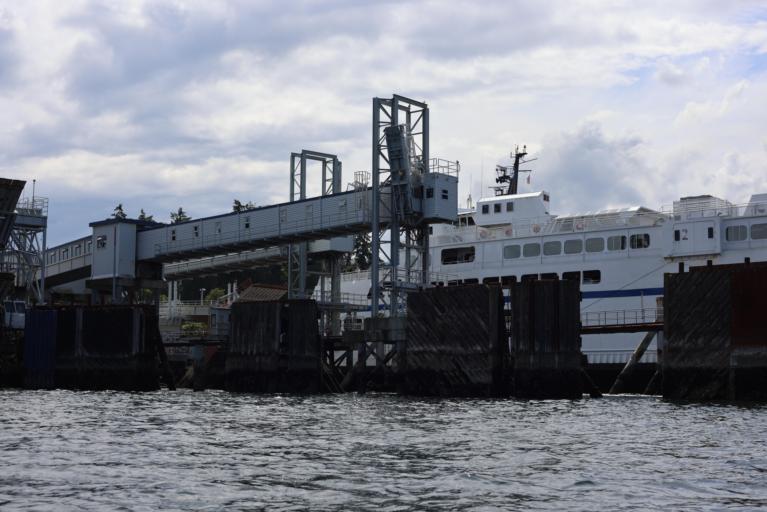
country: CA
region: British Columbia
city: Nanaimo
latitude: 49.1948
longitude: -123.9554
